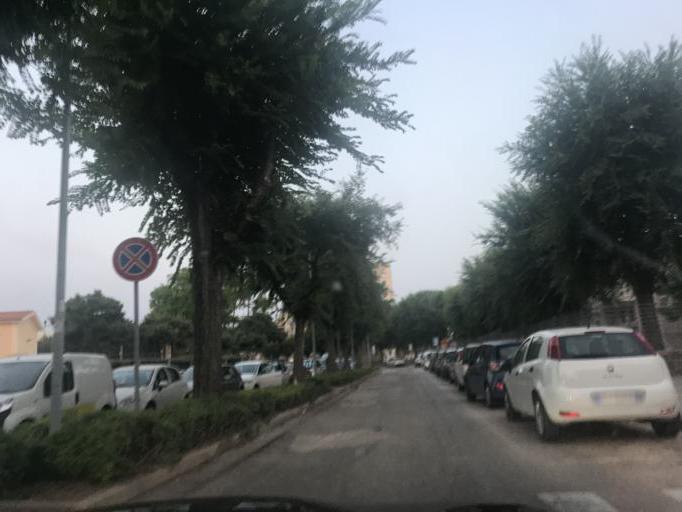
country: IT
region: Sardinia
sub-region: Provincia di Sassari
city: Alghero
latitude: 40.5564
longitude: 8.3180
